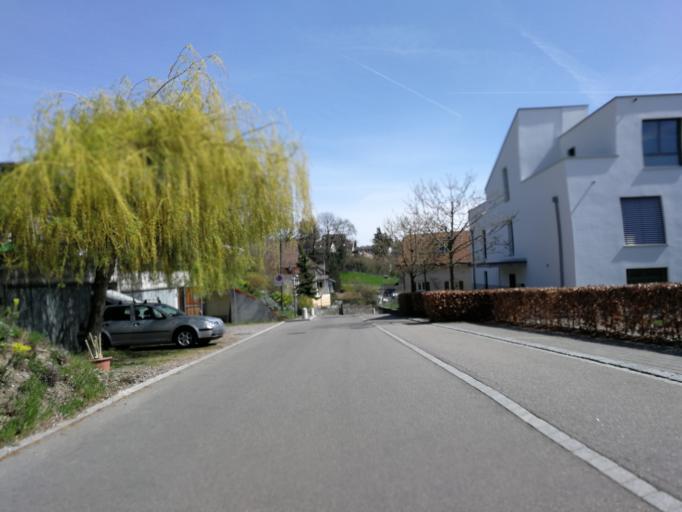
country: CH
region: Zurich
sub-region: Bezirk Meilen
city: Meilen
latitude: 47.2725
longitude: 8.6378
